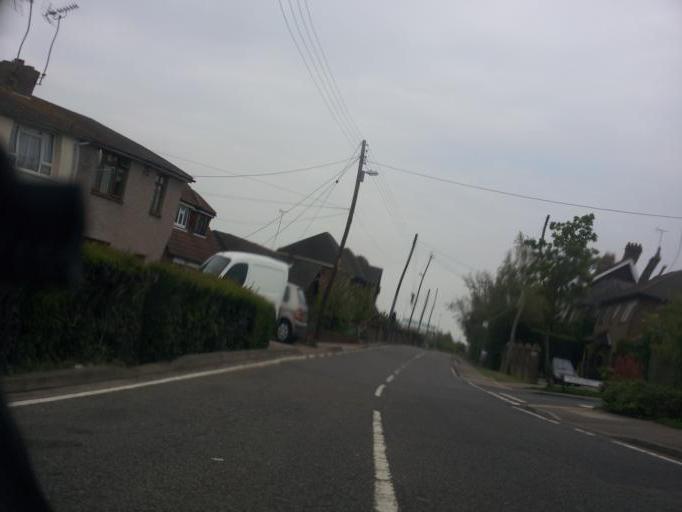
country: GB
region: England
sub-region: Kent
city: Hoo
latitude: 51.4196
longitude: 0.5351
